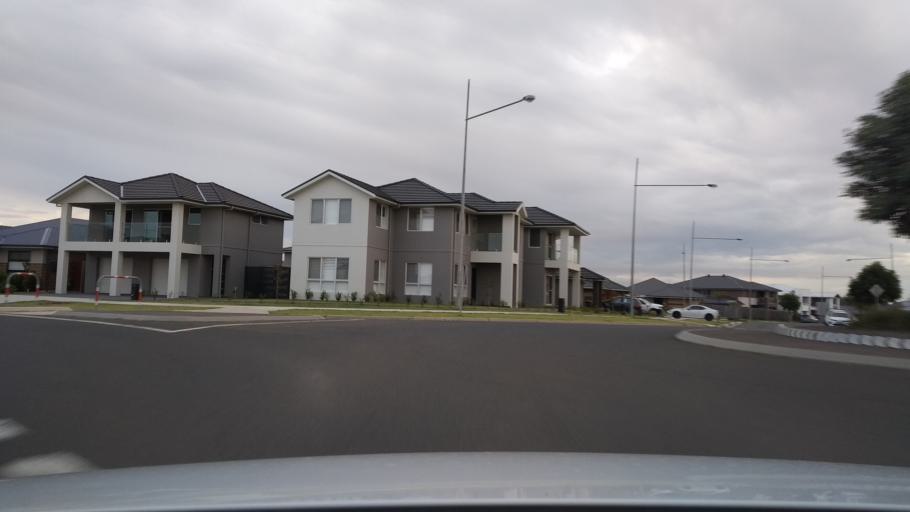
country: AU
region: New South Wales
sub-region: Camden
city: Narellan
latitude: -34.0067
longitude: 150.7358
